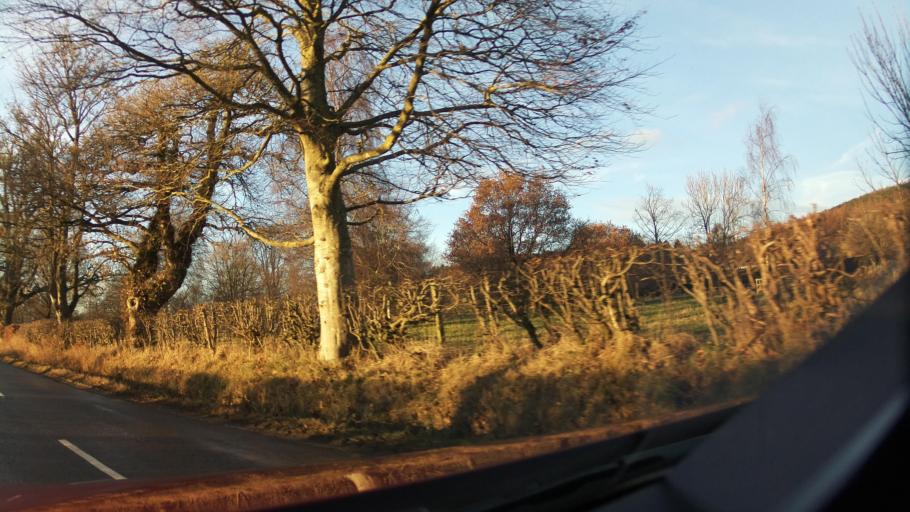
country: GB
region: Scotland
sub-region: Angus
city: Forfar
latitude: 56.5878
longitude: -2.8758
